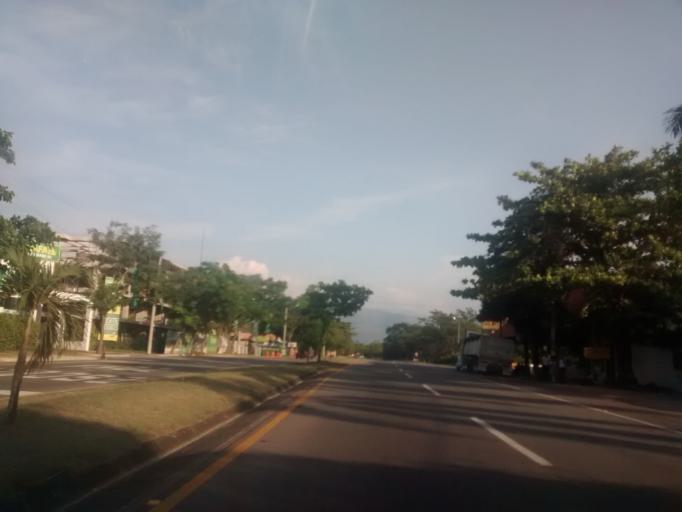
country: CO
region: Tolima
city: Melgar
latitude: 4.2238
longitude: -74.6963
